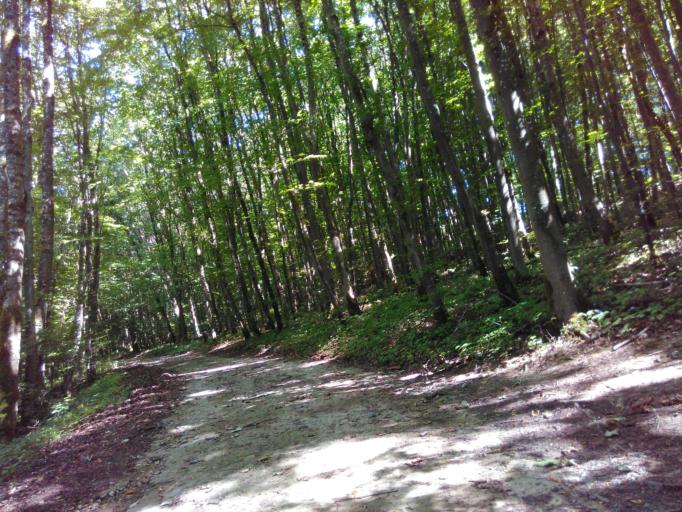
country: LU
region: Luxembourg
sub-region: Canton d'Esch-sur-Alzette
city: Leudelange
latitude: 49.5582
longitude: 6.0431
